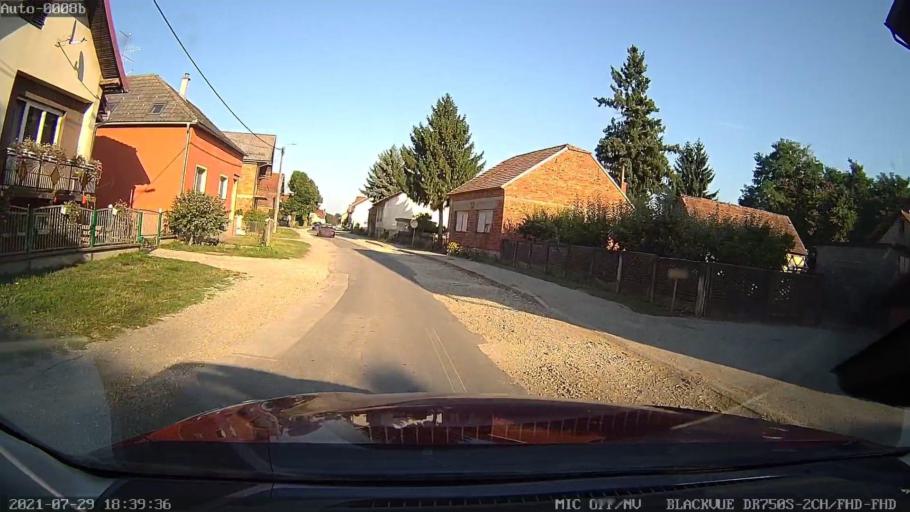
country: HR
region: Varazdinska
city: Petrijanec
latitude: 46.3213
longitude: 16.2236
